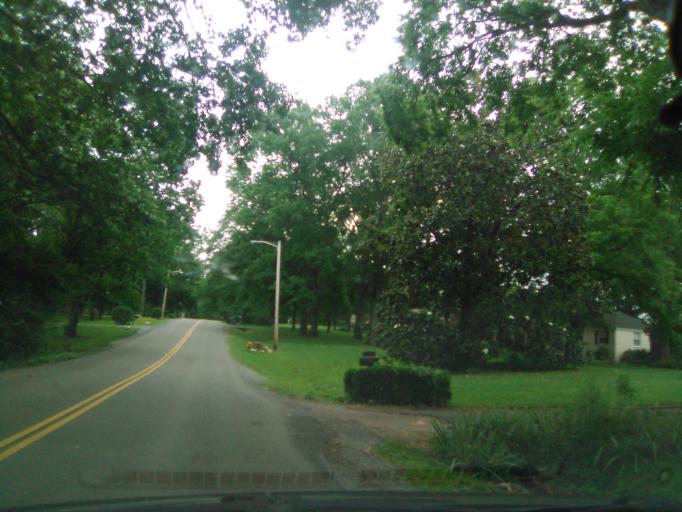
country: US
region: Tennessee
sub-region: Davidson County
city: Belle Meade
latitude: 36.1086
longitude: -86.8841
